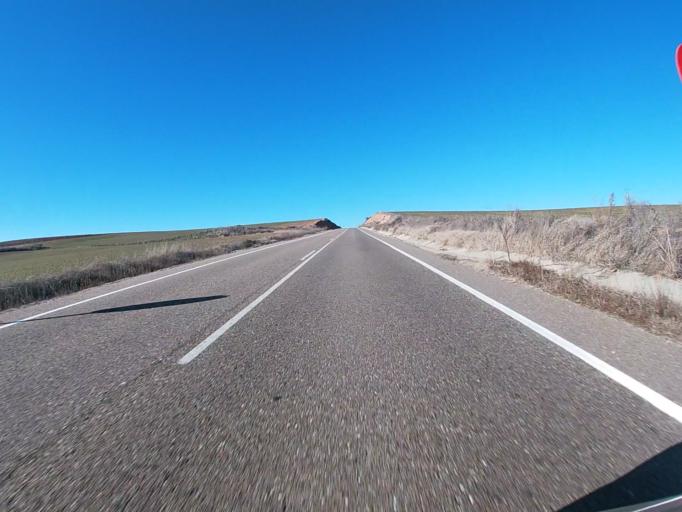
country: ES
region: Castille and Leon
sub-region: Provincia de Salamanca
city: Almenara de Tormes
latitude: 41.0703
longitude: -5.8293
